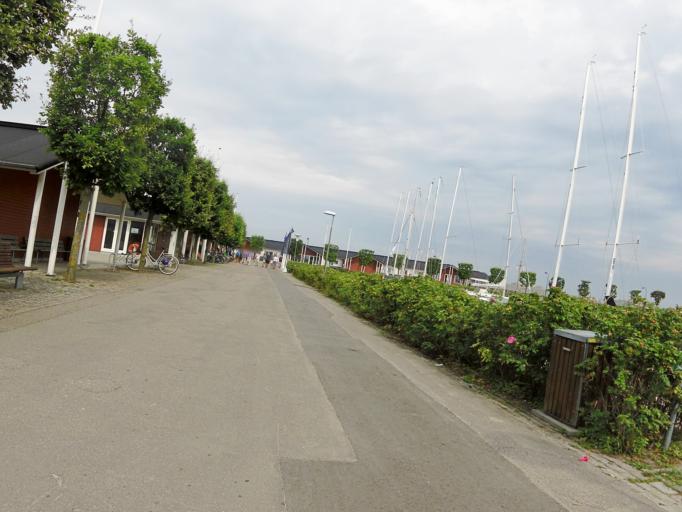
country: DK
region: Capital Region
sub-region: Gentofte Kommune
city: Charlottenlund
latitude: 55.7622
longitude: 12.5999
